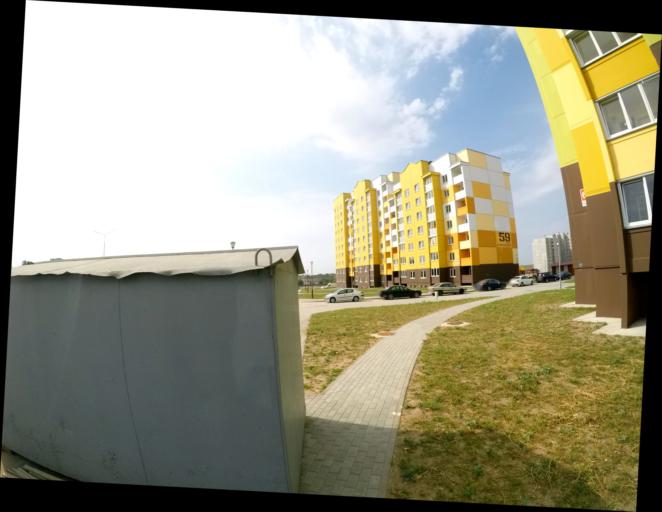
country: BY
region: Grodnenskaya
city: Hrodna
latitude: 53.7175
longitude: 23.8653
